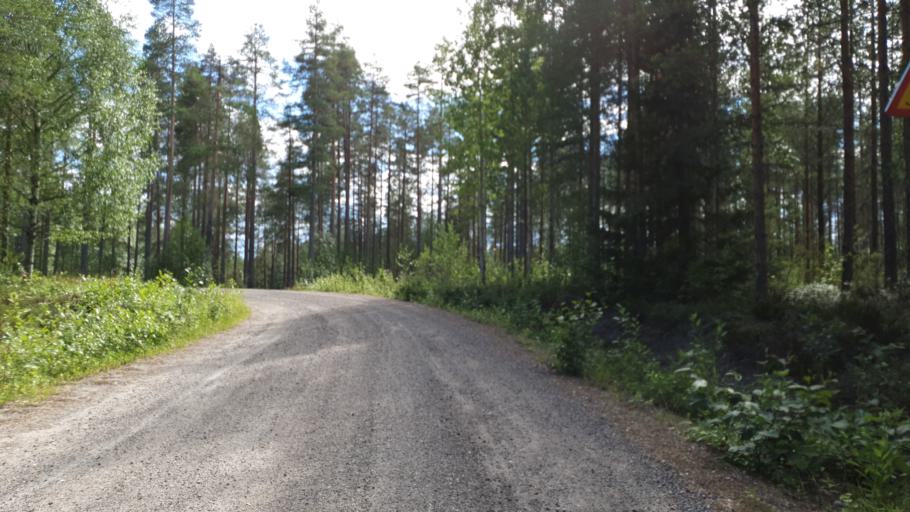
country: FI
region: Kainuu
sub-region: Kehys-Kainuu
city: Kuhmo
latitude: 64.1153
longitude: 29.5166
